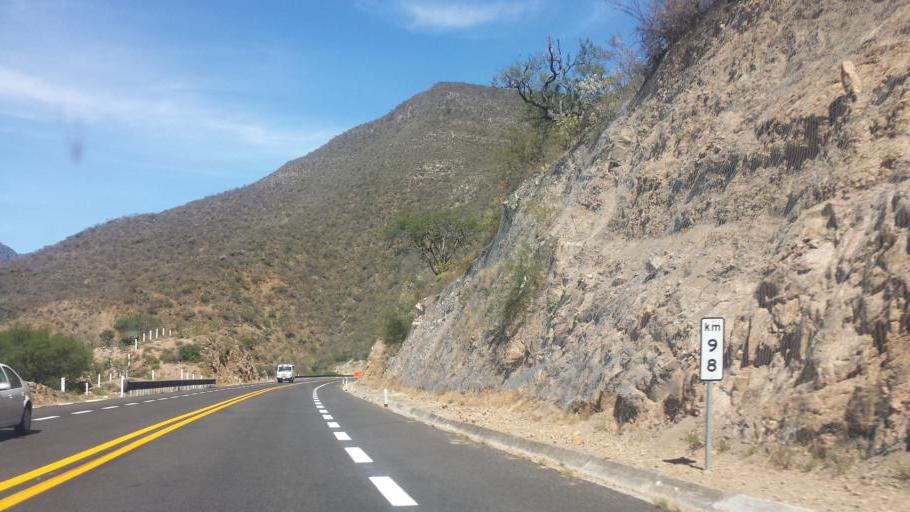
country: MX
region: Puebla
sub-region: San Jose Miahuatlan
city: San Pedro Tetitlan
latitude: 18.0999
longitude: -97.3365
